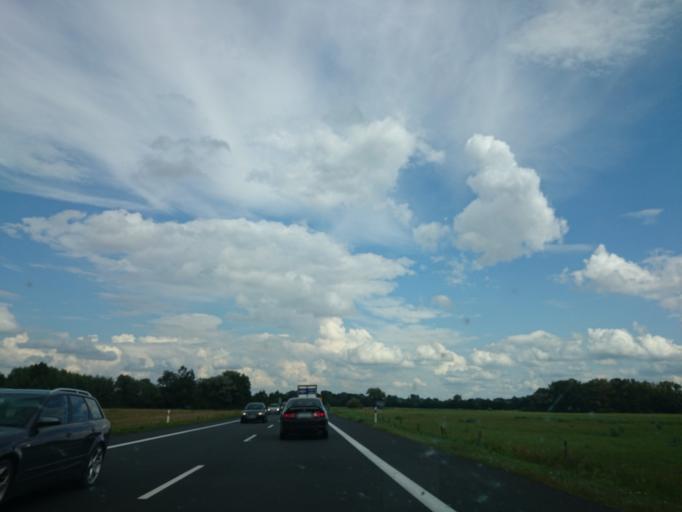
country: PL
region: Lubusz
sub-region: Powiat zielonogorski
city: Sulechow
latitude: 52.0092
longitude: 15.6115
